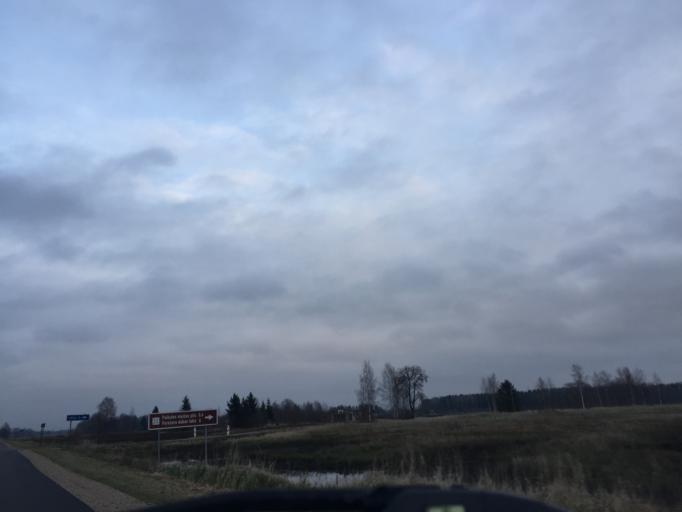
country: LV
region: Aloja
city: Aloja
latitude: 57.6923
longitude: 24.8783
